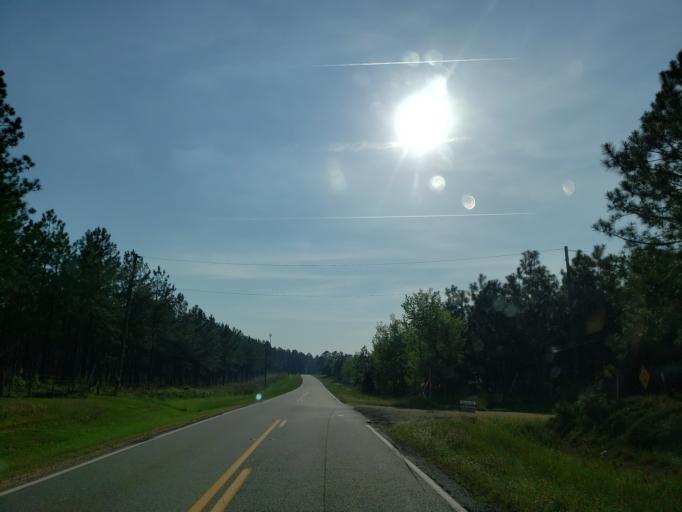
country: US
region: Georgia
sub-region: Tift County
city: Tifton
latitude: 31.5529
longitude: -83.5255
